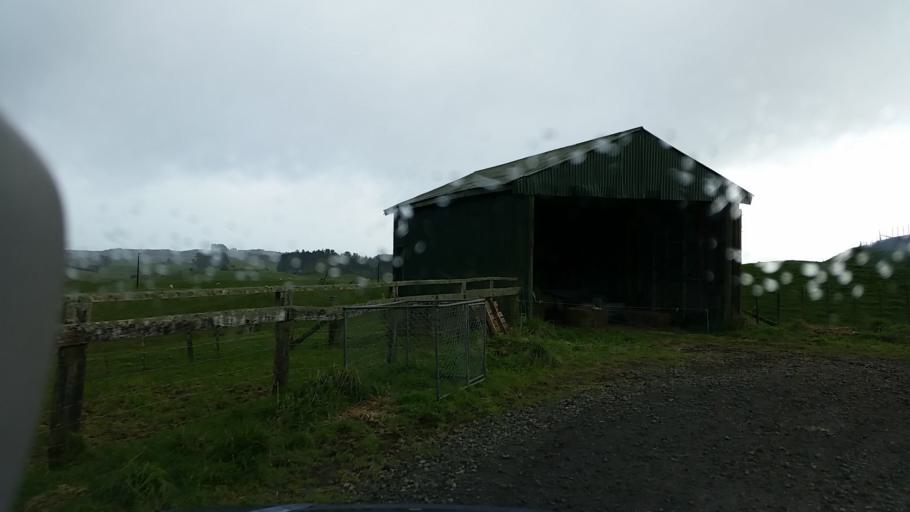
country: NZ
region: Taranaki
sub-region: South Taranaki District
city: Eltham
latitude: -39.2750
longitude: 174.3389
